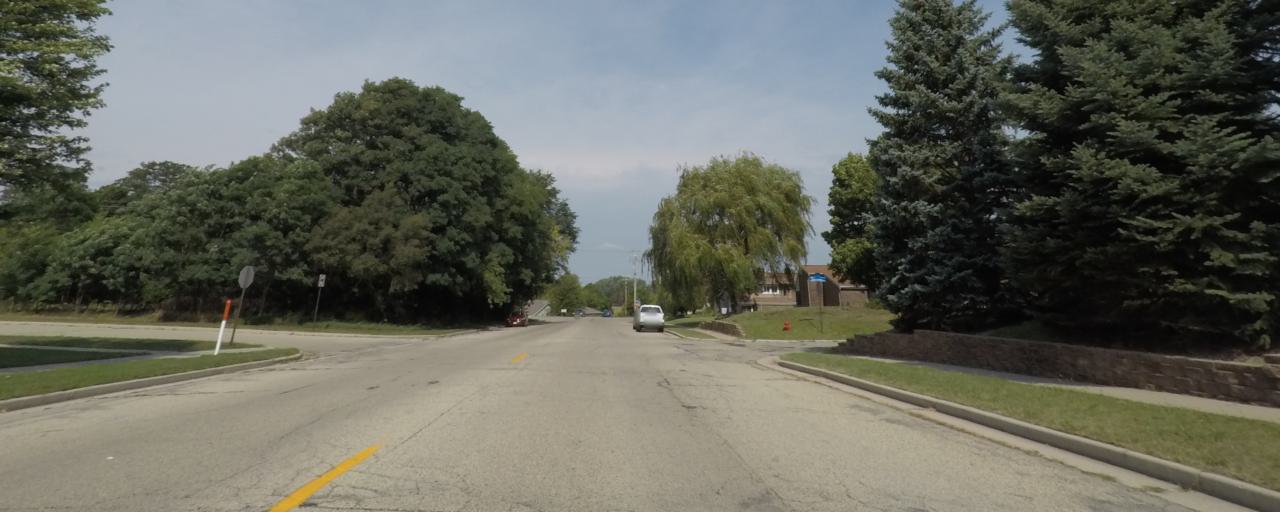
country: US
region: Wisconsin
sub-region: Jefferson County
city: Jefferson
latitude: 42.9913
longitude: -88.8241
